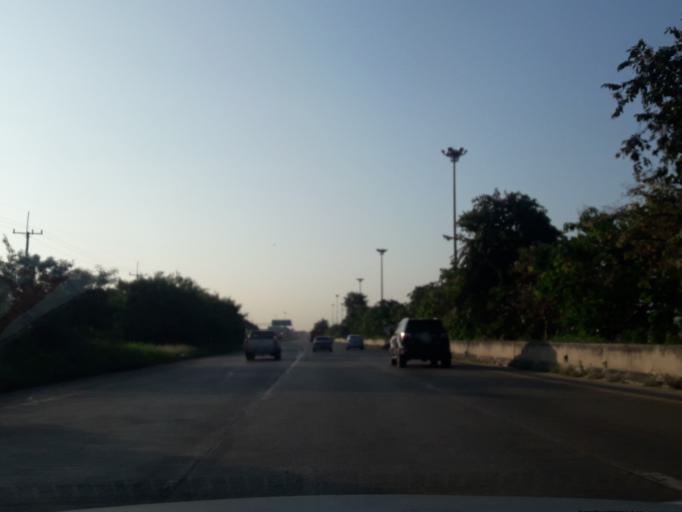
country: TH
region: Phra Nakhon Si Ayutthaya
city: Bang Pa-in
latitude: 14.1639
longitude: 100.5650
